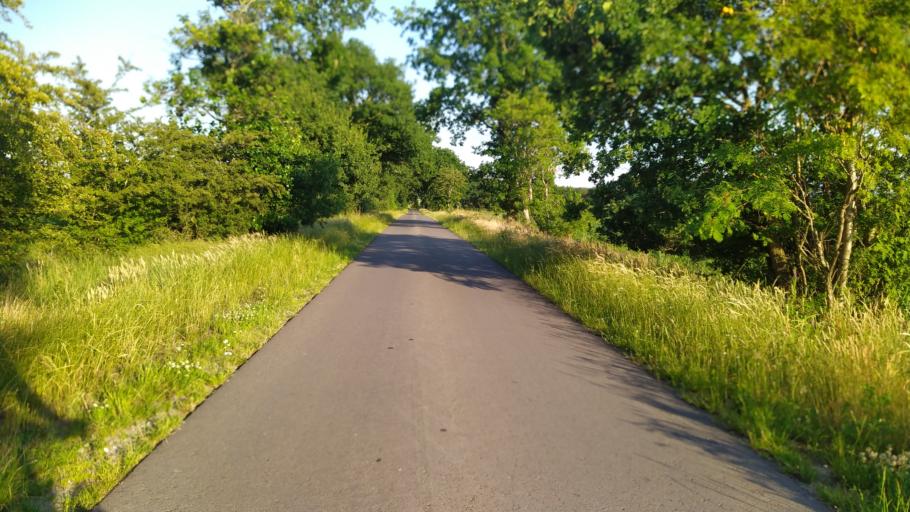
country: DE
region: Lower Saxony
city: Alfstedt
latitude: 53.5668
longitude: 9.0277
